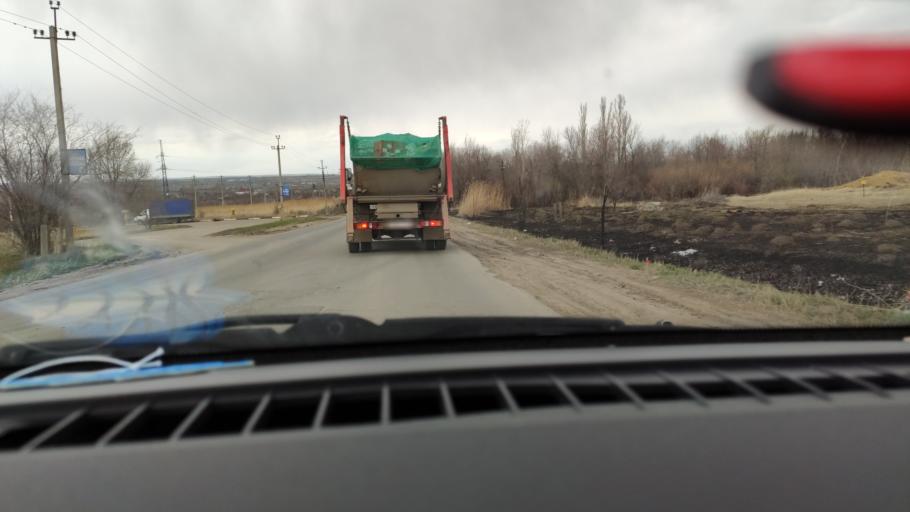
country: RU
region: Saratov
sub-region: Saratovskiy Rayon
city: Saratov
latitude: 51.6191
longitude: 45.9462
